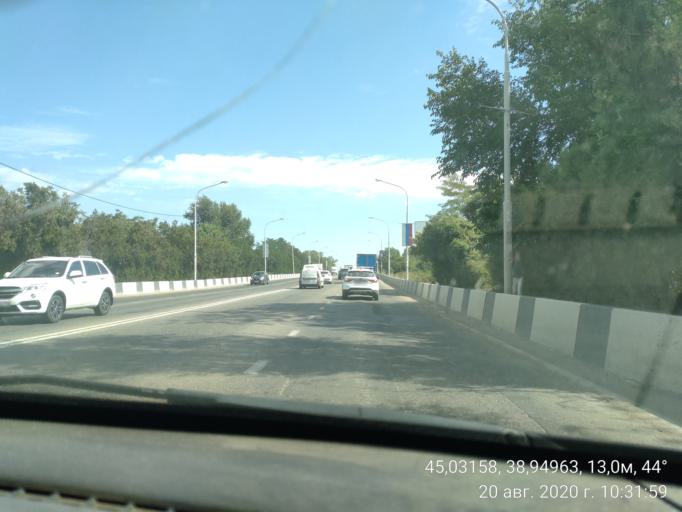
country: RU
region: Krasnodarskiy
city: Krasnodar
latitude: 45.0316
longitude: 38.9496
